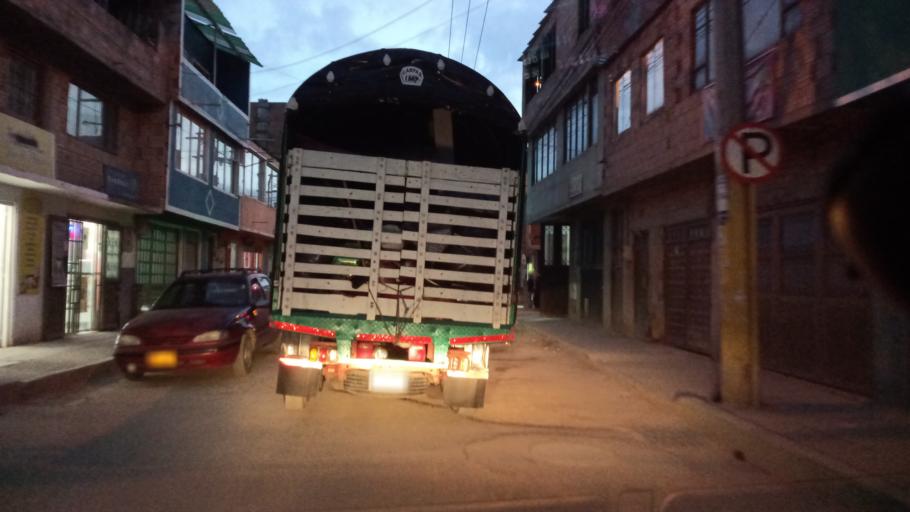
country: CO
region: Cundinamarca
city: Soacha
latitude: 4.5707
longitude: -74.2325
